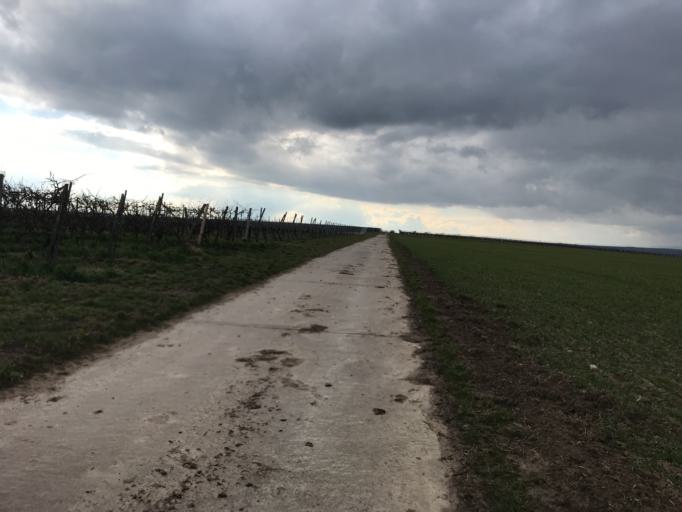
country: DE
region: Rheinland-Pfalz
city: Essenheim
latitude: 49.9015
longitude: 8.1725
